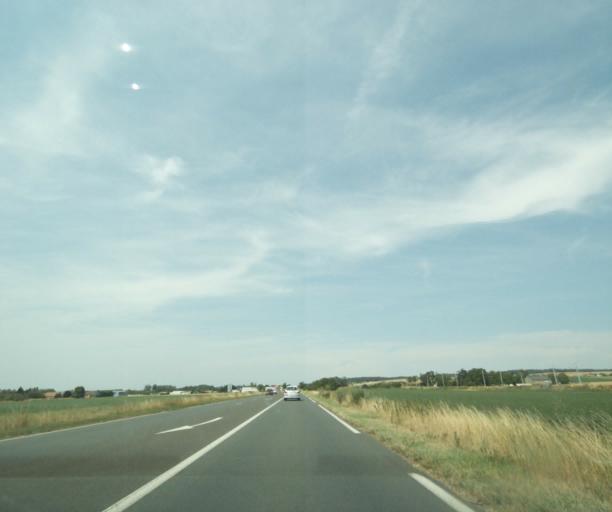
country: FR
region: Poitou-Charentes
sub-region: Departement de la Vienne
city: Les Ormes
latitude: 46.9538
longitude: 0.6075
